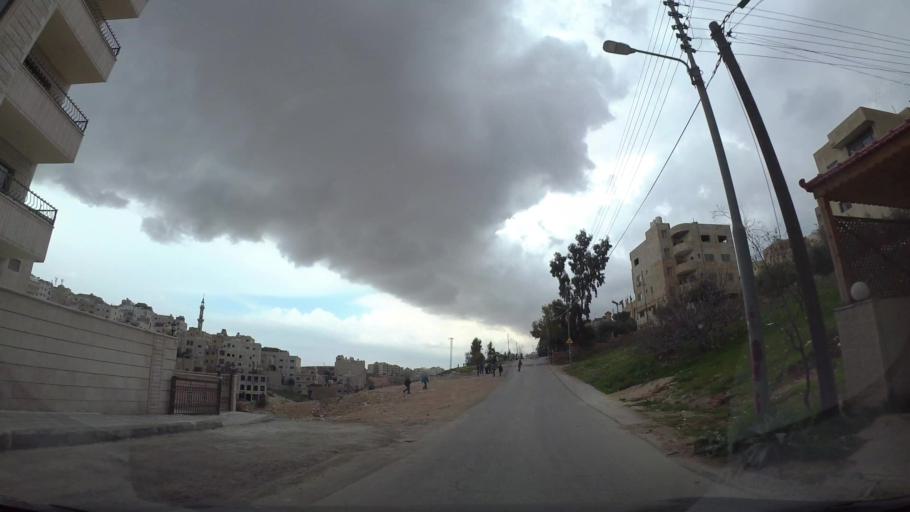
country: JO
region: Amman
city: Amman
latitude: 32.0093
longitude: 35.9467
